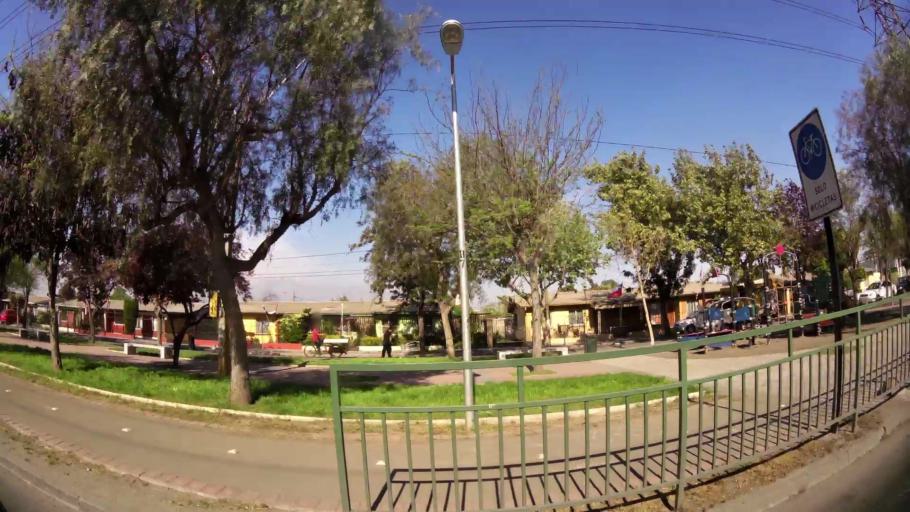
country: CL
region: Santiago Metropolitan
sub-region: Provincia de Santiago
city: Santiago
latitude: -33.4955
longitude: -70.6771
